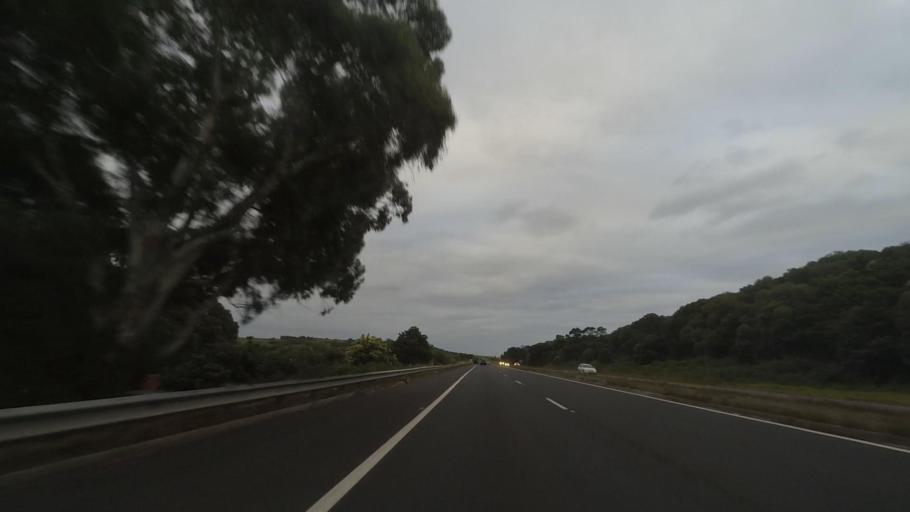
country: AU
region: New South Wales
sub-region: Kiama
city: Kiama
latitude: -34.6683
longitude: 150.8447
